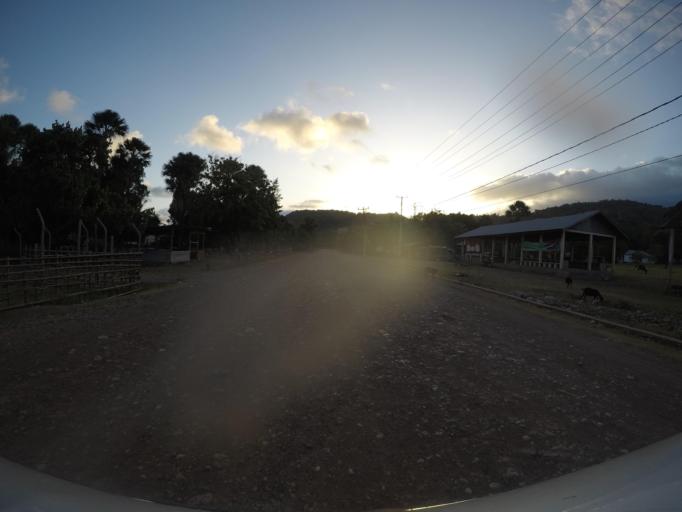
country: TL
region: Baucau
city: Venilale
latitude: -8.7499
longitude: 126.6973
